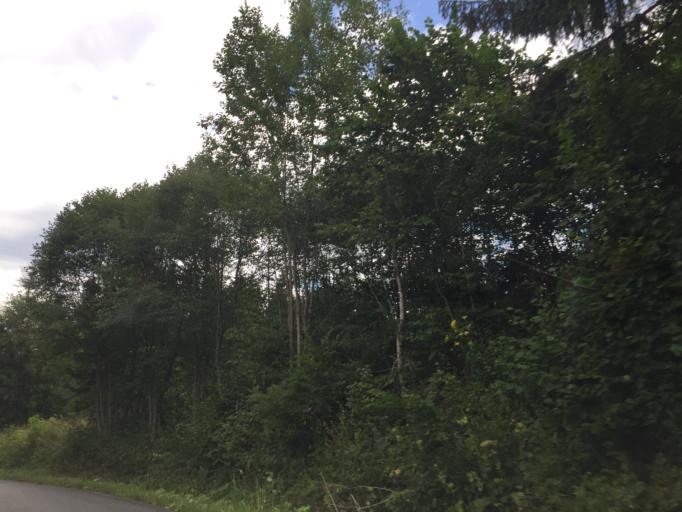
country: SK
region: Zilinsky
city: Namestovo
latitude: 49.4180
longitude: 19.3327
